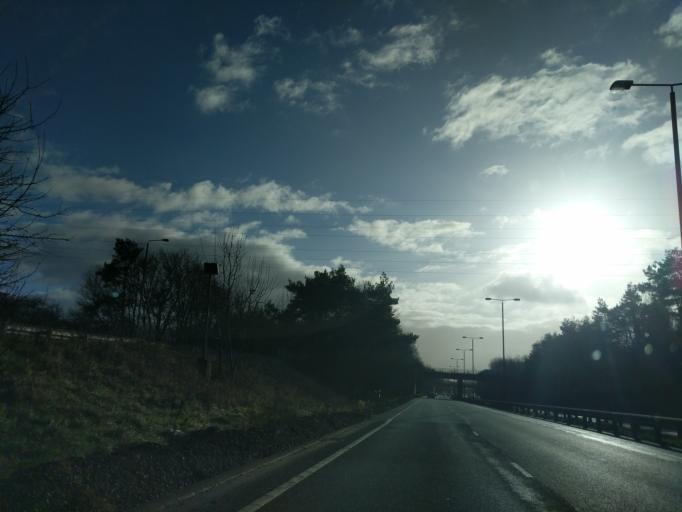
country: GB
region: England
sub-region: Derbyshire
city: Findern
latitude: 52.8881
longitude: -1.5438
